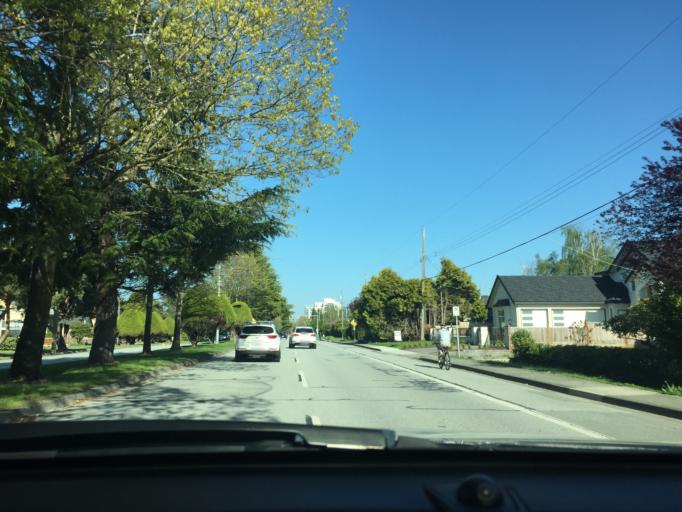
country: CA
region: British Columbia
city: Richmond
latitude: 49.1627
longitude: -123.1561
